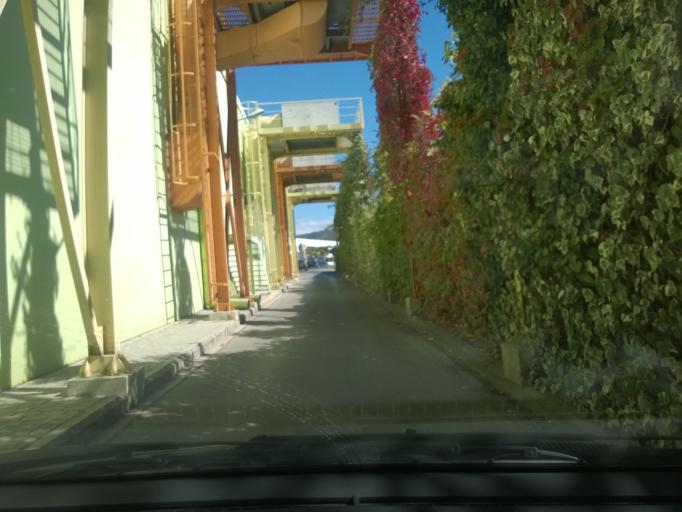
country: GR
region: Central Macedonia
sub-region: Nomos Thessalonikis
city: Efkarpia
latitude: 40.6910
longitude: 22.9407
